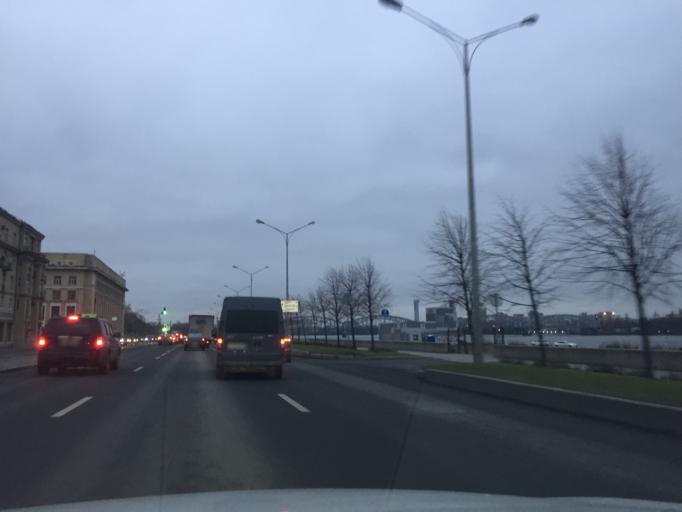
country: RU
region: St.-Petersburg
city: Centralniy
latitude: 59.9227
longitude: 30.4054
